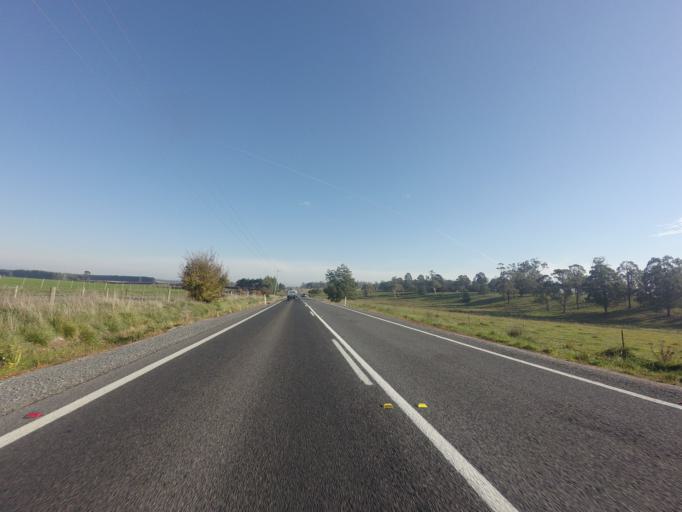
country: AU
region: Tasmania
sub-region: Northern Midlands
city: Longford
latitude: -41.5691
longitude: 147.0907
